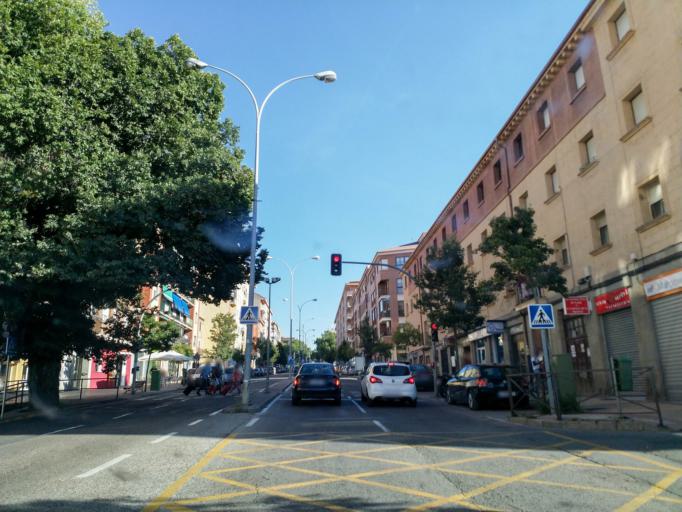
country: ES
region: Castille and Leon
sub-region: Provincia de Segovia
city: Segovia
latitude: 40.9464
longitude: -4.1233
